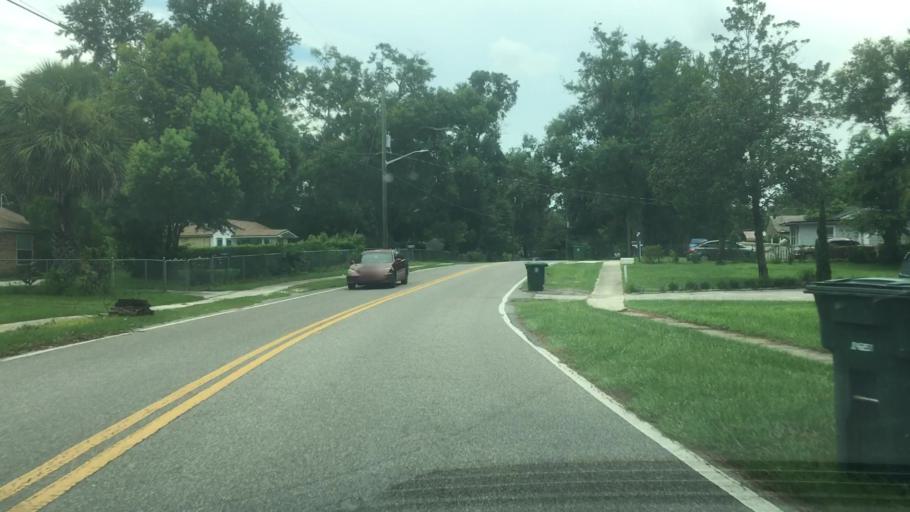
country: US
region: Florida
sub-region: Duval County
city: Jacksonville
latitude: 30.3034
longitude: -81.5493
